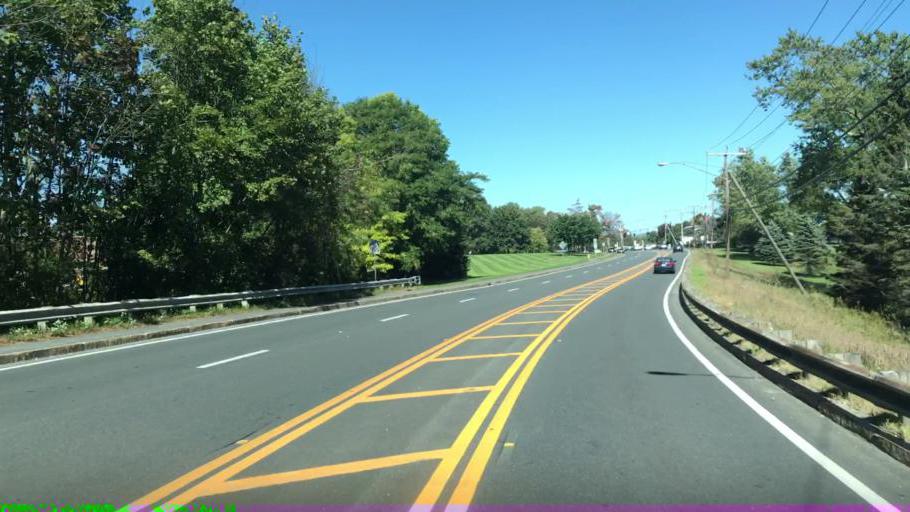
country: US
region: Massachusetts
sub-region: Berkshire County
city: Pittsfield
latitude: 42.4236
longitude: -73.2609
